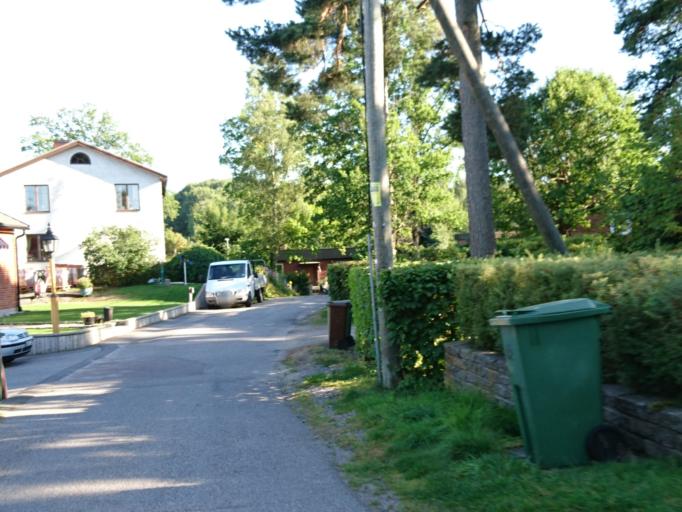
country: SE
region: Stockholm
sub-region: Huddinge Kommun
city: Segeltorp
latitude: 59.2755
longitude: 17.9399
